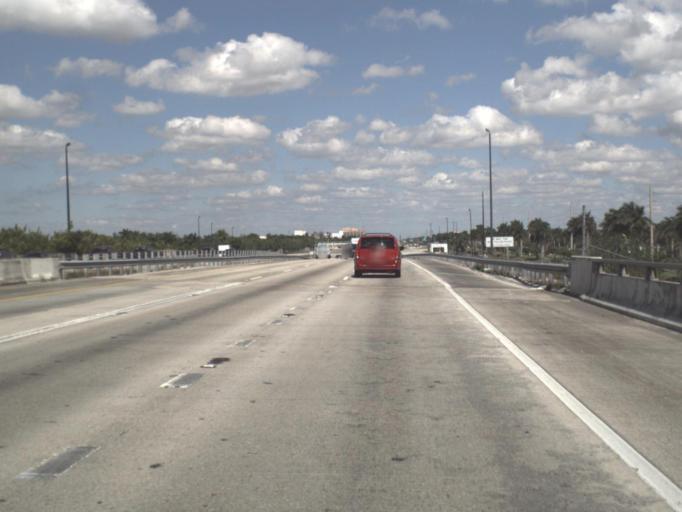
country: US
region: Florida
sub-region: Miami-Dade County
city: Westwood Lake
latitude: 25.7151
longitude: -80.3834
